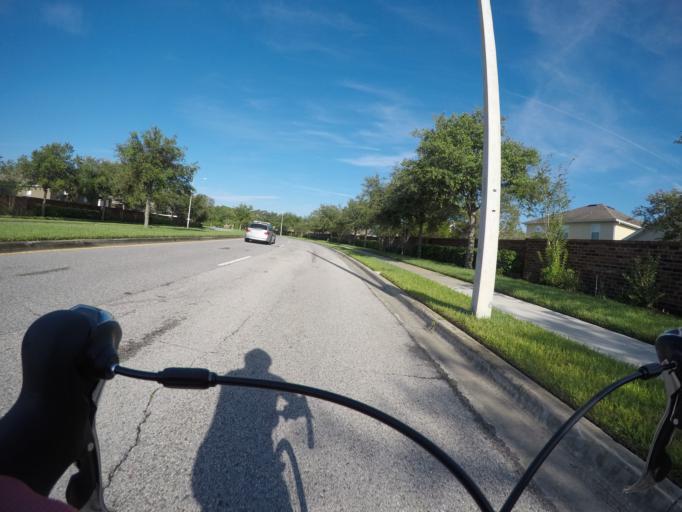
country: US
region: Florida
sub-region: Osceola County
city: Buenaventura Lakes
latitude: 28.3593
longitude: -81.3385
